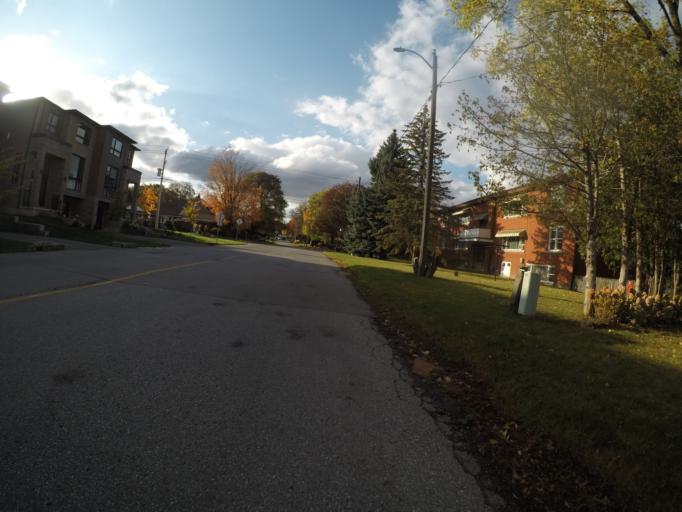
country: CA
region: Ontario
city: Kitchener
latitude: 43.4371
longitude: -80.4620
